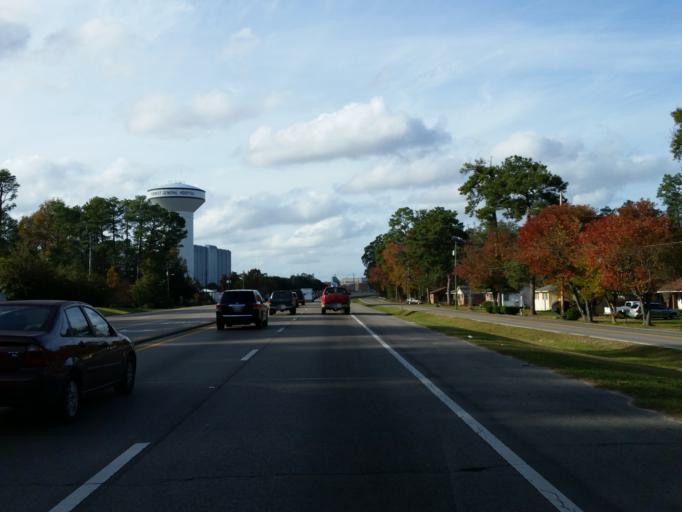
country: US
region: Mississippi
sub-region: Forrest County
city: Hattiesburg
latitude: 31.3155
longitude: -89.3251
